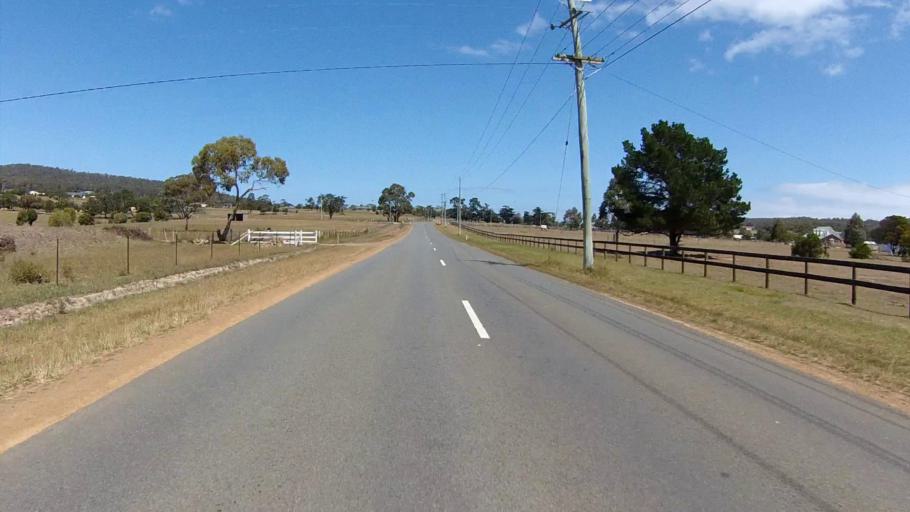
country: AU
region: Tasmania
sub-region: Clarence
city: Sandford
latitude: -42.9498
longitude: 147.4813
